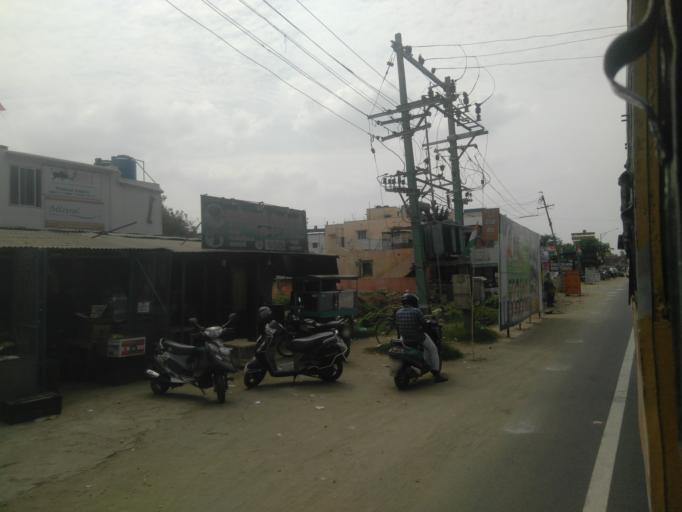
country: IN
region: Tamil Nadu
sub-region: Coimbatore
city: Irugur
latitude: 11.0075
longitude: 77.0723
